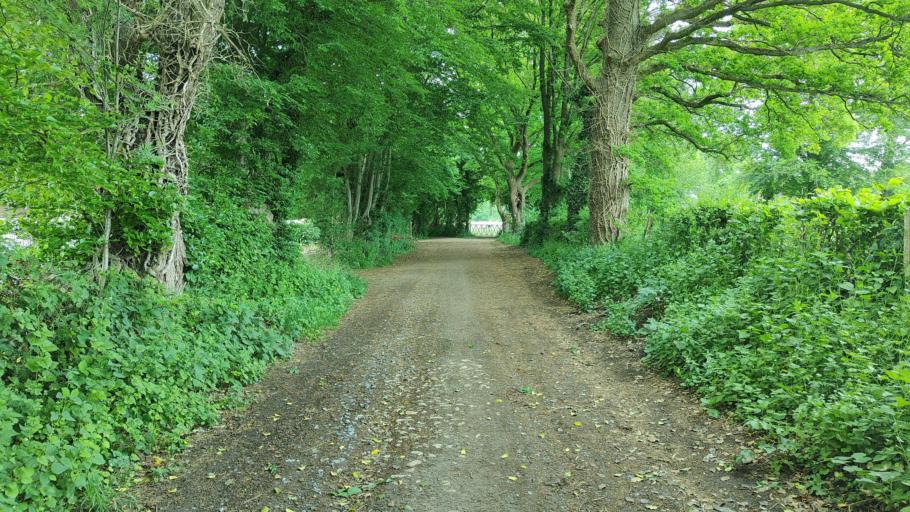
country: BE
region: Wallonia
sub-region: Province de Liege
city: La Calamine
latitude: 50.7171
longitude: 6.0676
